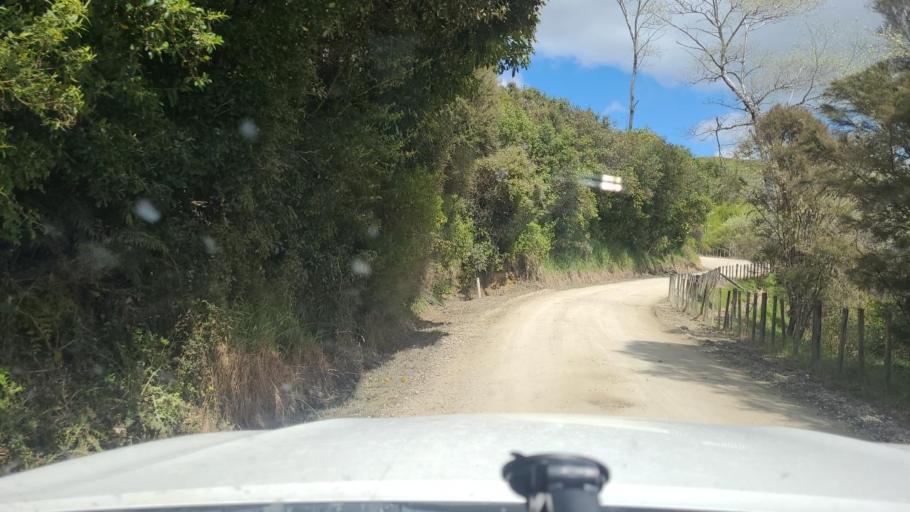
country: NZ
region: Gisborne
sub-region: Gisborne District
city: Gisborne
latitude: -38.8269
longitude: 177.7375
